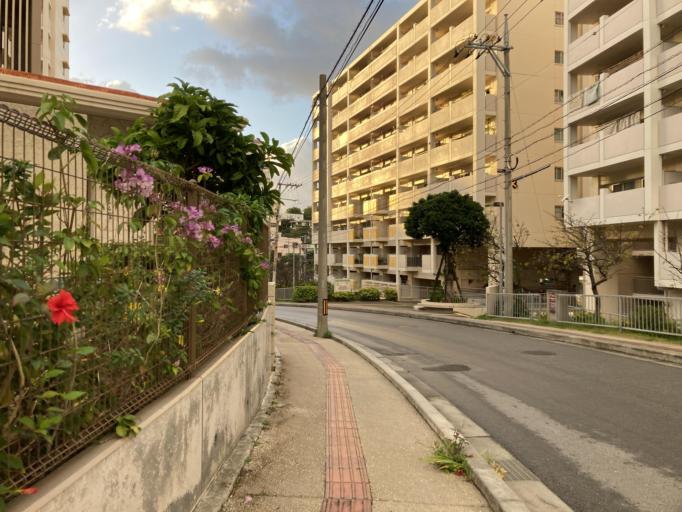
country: JP
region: Okinawa
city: Naha-shi
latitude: 26.2222
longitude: 127.7258
